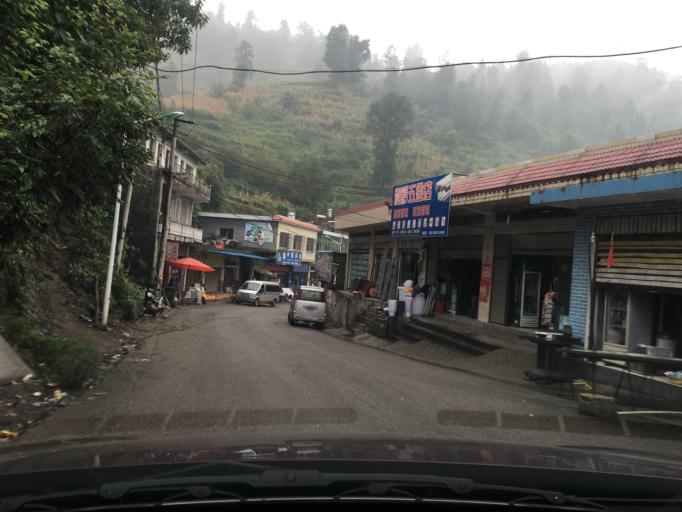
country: CN
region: Guizhou Sheng
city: Liupanshui
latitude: 26.0565
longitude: 105.1212
